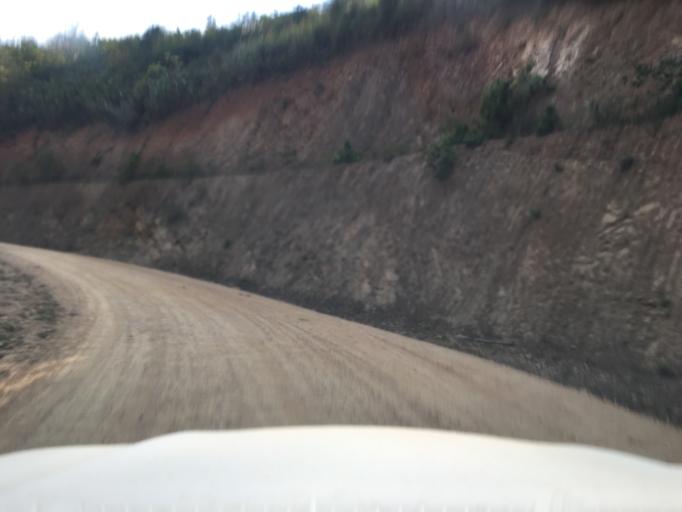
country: LA
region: Houaphan
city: Huameung
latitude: 20.2049
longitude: 103.8497
